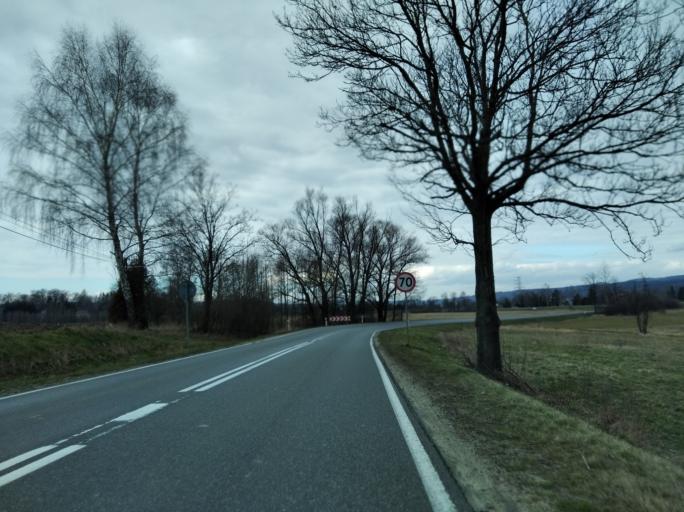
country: PL
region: Subcarpathian Voivodeship
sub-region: Powiat krosnienski
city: Wojaszowka
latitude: 49.7882
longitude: 21.6599
